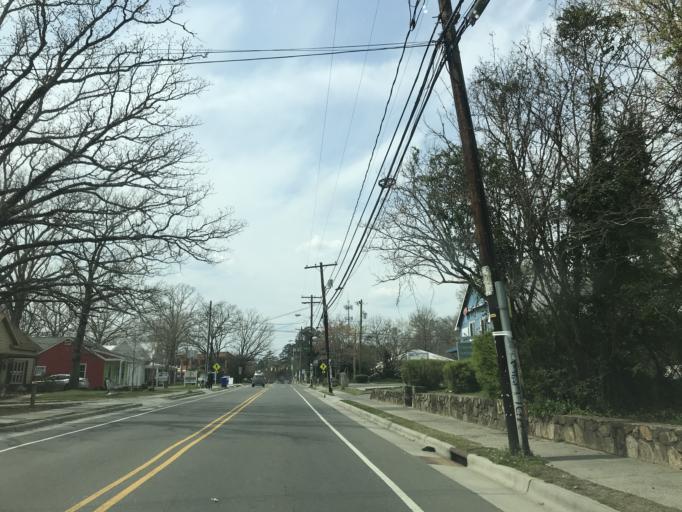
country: US
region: North Carolina
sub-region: Orange County
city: Carrboro
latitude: 35.9112
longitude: -79.0744
